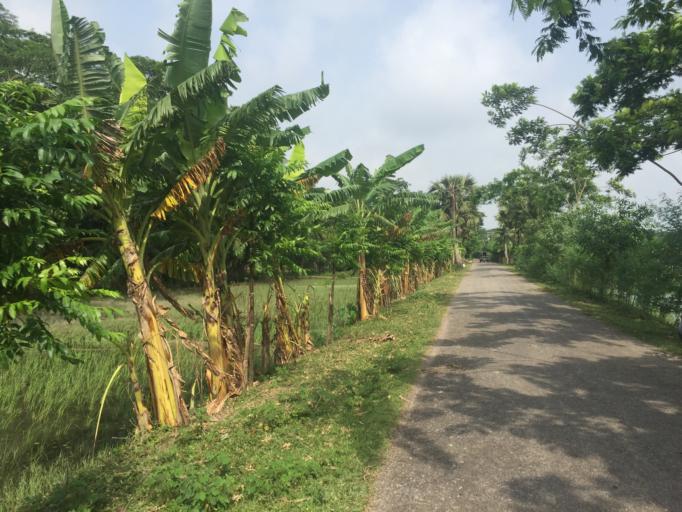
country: BD
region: Barisal
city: Mathba
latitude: 22.2525
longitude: 89.9154
